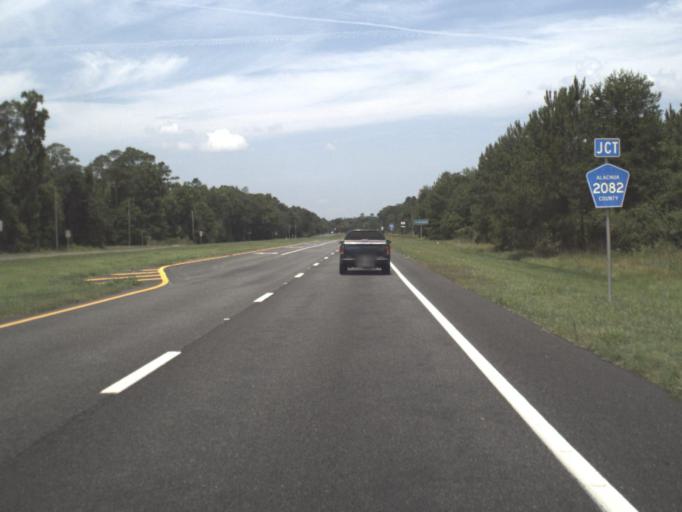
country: US
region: Florida
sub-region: Alachua County
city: Gainesville
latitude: 29.6097
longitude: -82.2396
